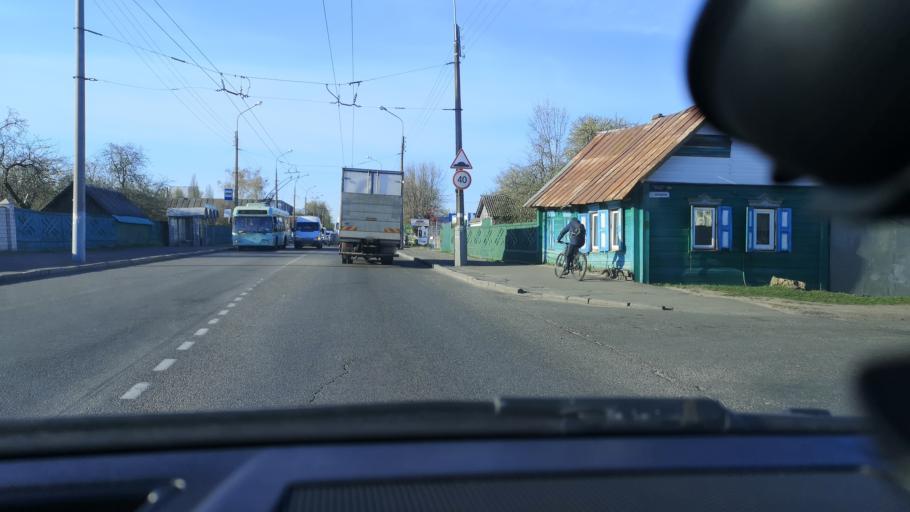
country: BY
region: Gomel
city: Gomel
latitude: 52.4249
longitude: 30.9738
